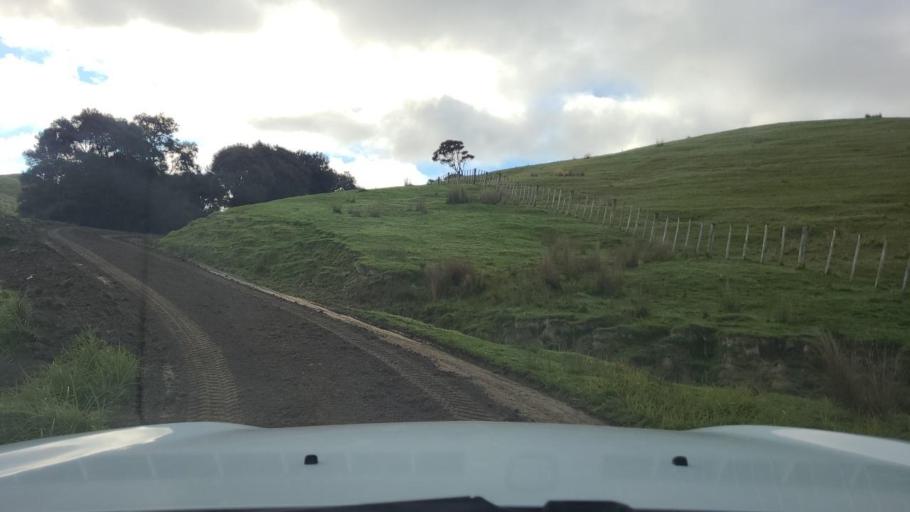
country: NZ
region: Wellington
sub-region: South Wairarapa District
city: Waipawa
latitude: -41.2401
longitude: 175.6816
